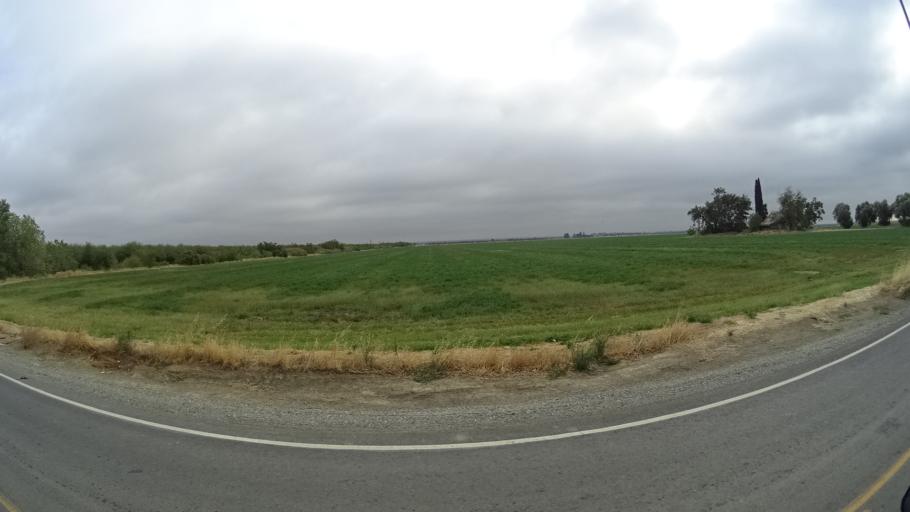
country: US
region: California
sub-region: Yolo County
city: Esparto
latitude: 38.7591
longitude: -122.0444
